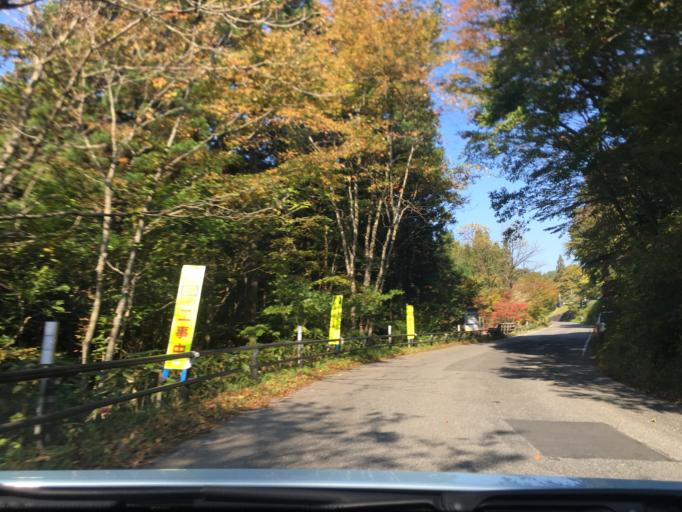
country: JP
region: Fukushima
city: Sukagawa
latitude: 37.3054
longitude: 140.1462
